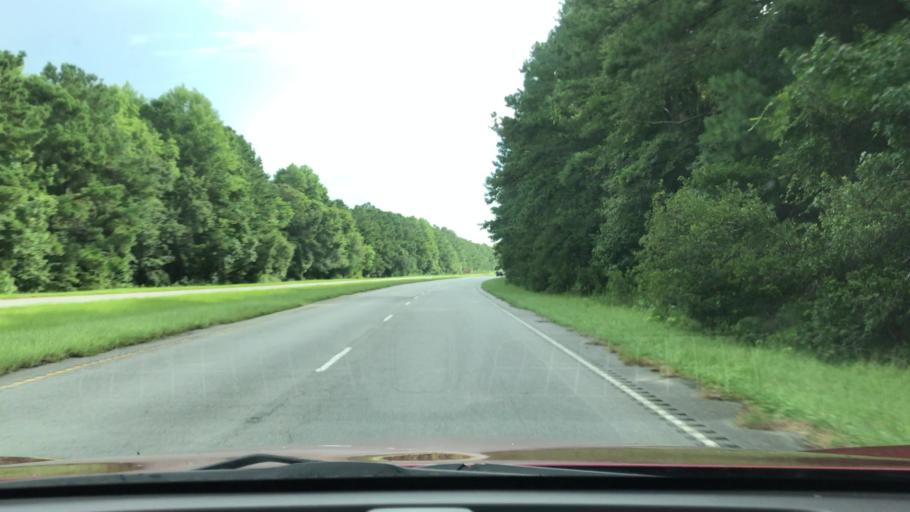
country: US
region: South Carolina
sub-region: Charleston County
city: Awendaw
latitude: 32.9711
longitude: -79.6751
